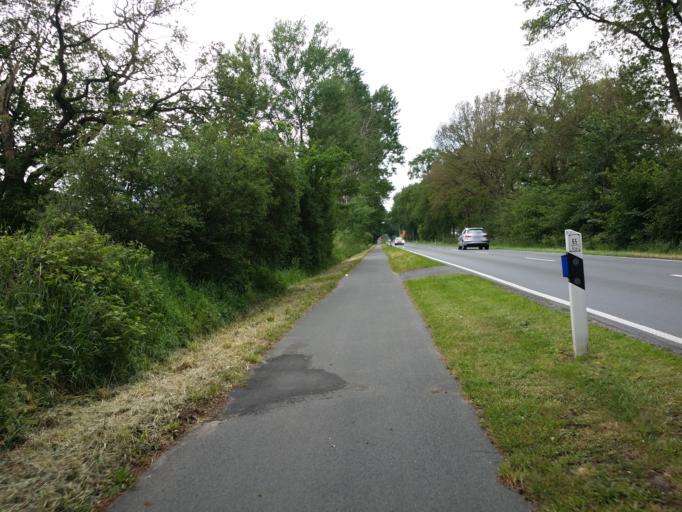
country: DE
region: Lower Saxony
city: Wittmund
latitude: 53.5333
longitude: 7.7818
